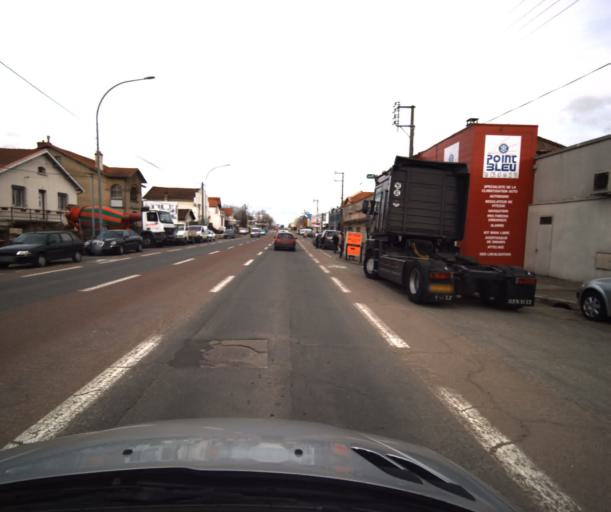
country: FR
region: Midi-Pyrenees
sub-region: Departement du Tarn-et-Garonne
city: Montauban
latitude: 44.0278
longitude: 1.3683
